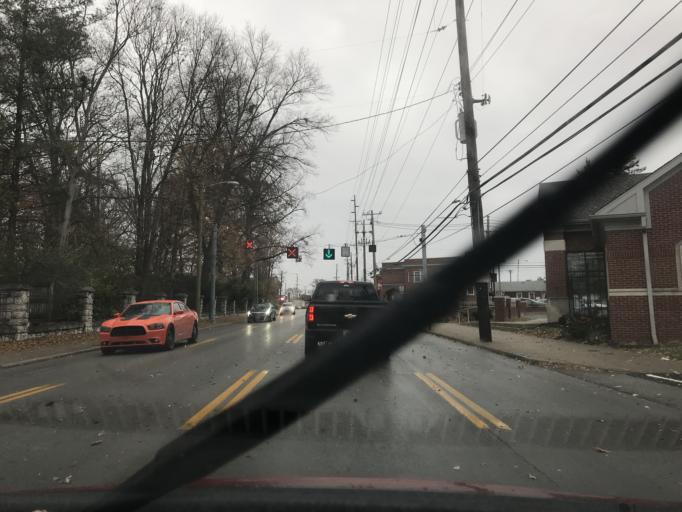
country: US
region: Kentucky
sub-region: Jefferson County
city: Audubon Park
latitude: 38.2255
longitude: -85.6961
